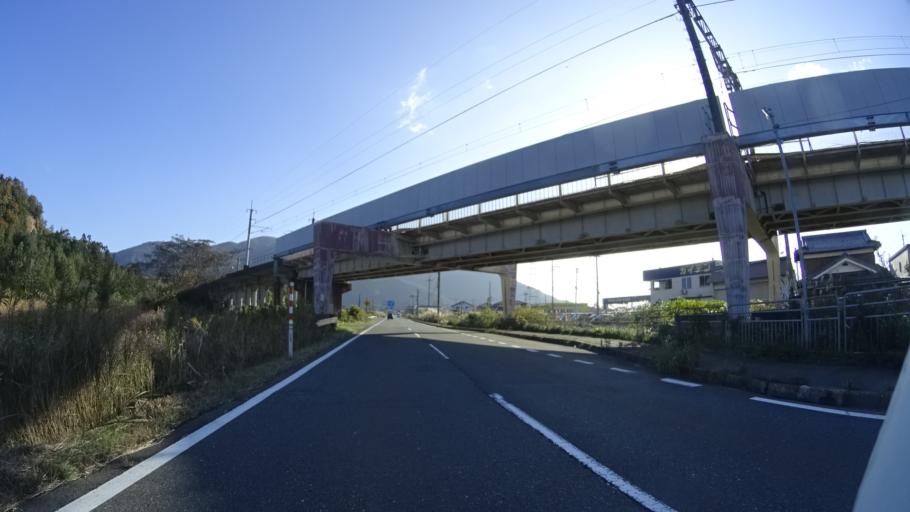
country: JP
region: Fukui
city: Tsuruga
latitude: 35.4622
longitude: 136.0609
